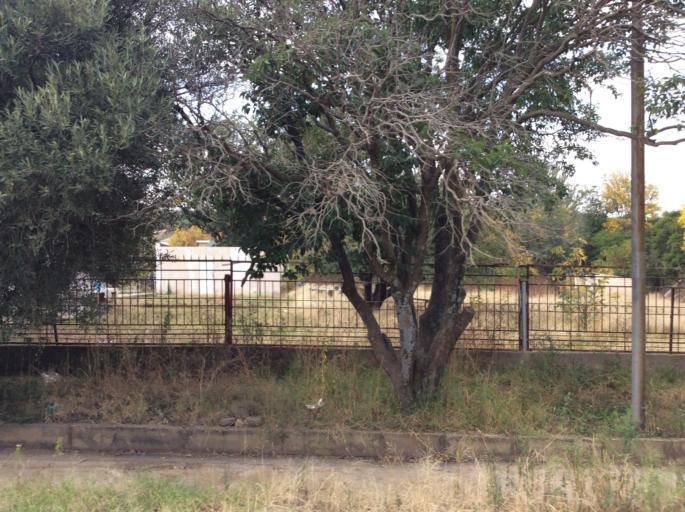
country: LS
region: Mafeteng
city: Mafeteng
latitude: -29.7299
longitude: 27.0409
